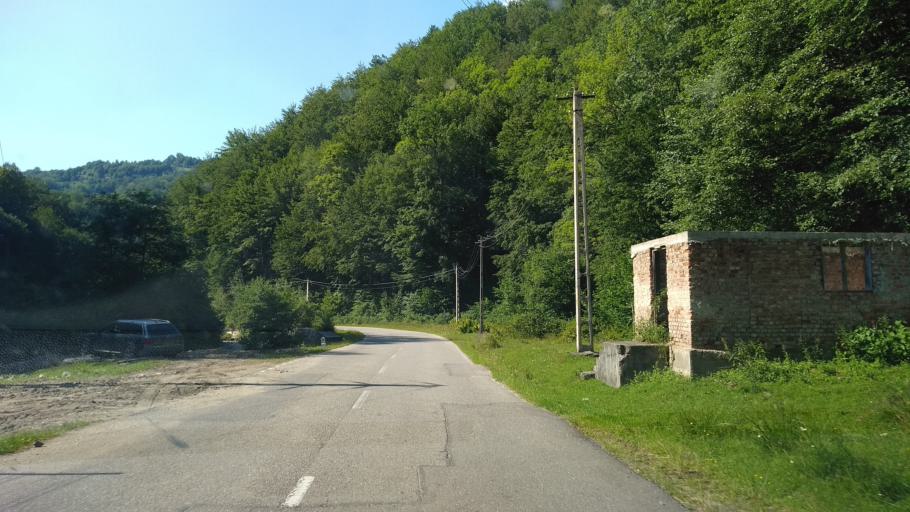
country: RO
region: Hunedoara
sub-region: Comuna Orastioara de Sus
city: Orastioara de Sus
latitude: 45.6288
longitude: 23.2185
